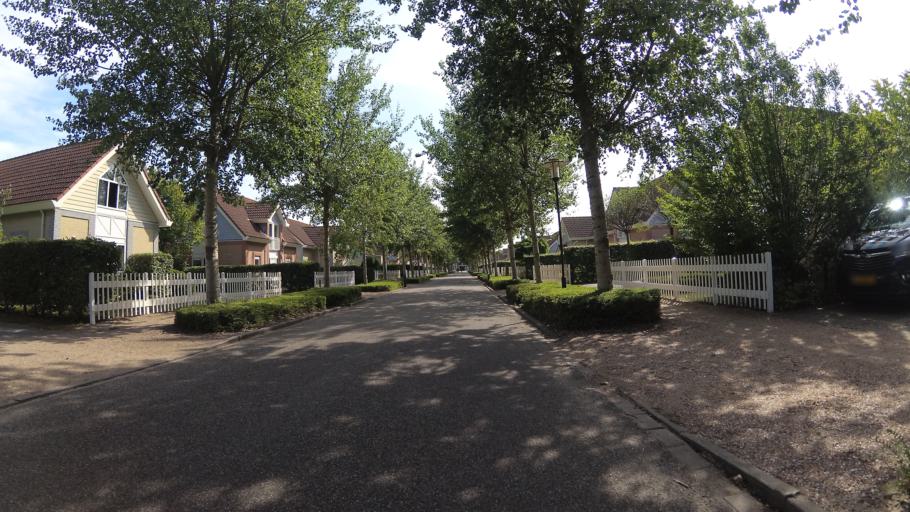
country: NL
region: Zeeland
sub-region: Gemeente Noord-Beveland
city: Kamperland
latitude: 51.5938
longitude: 3.6740
